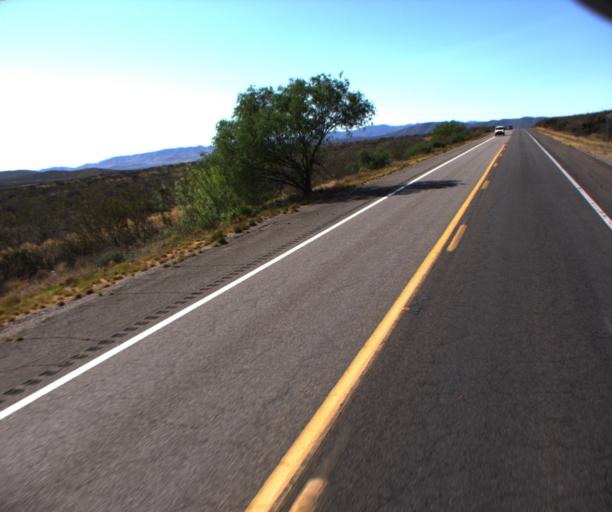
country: US
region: Arizona
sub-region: Cochise County
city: Tombstone
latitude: 31.6834
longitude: -110.0333
